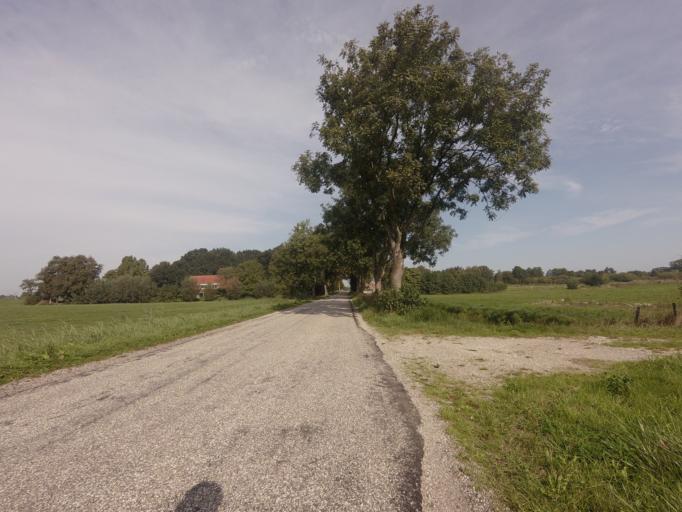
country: NL
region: Groningen
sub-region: Gemeente Leek
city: Leek
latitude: 53.2002
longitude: 6.3509
